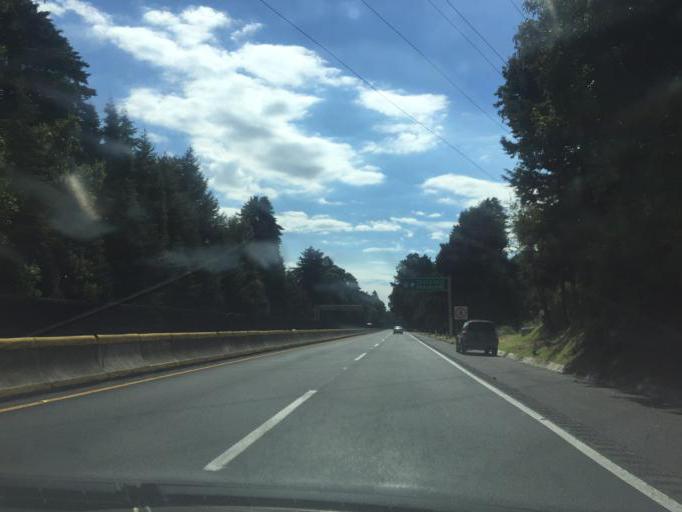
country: MX
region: Morelos
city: Tres Marias
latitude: 19.0459
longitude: -99.2359
